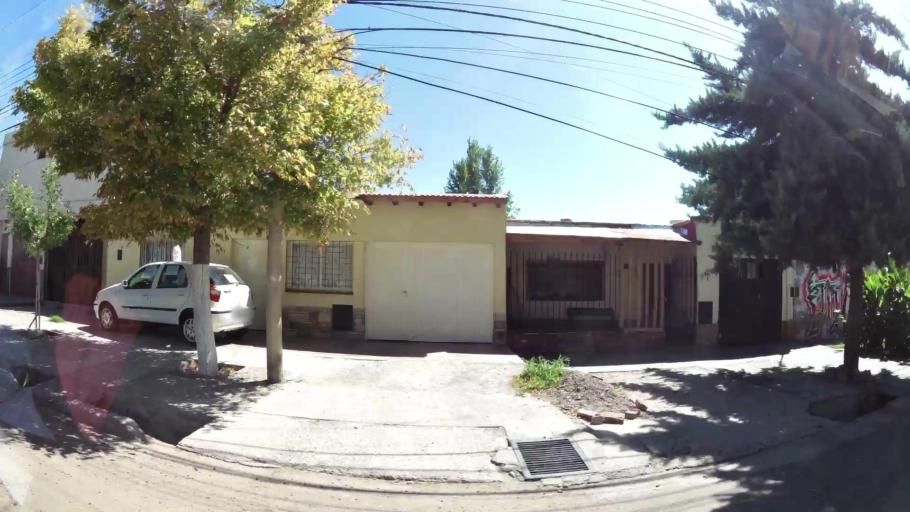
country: AR
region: Mendoza
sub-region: Departamento de Godoy Cruz
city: Godoy Cruz
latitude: -32.9390
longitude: -68.8521
